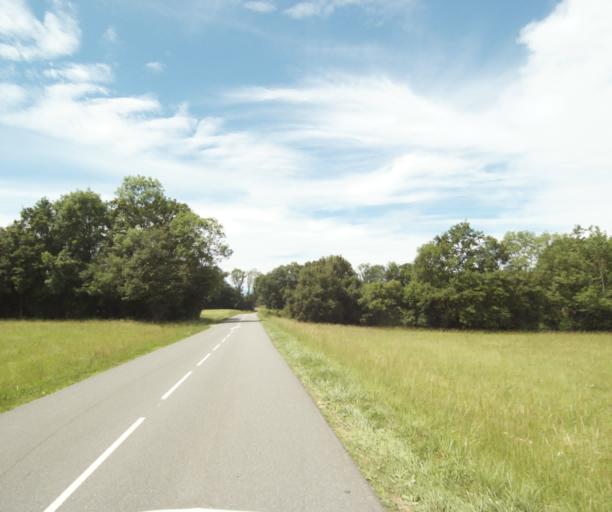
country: FR
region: Rhone-Alpes
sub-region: Departement de la Haute-Savoie
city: Margencel
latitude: 46.3298
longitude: 6.4350
